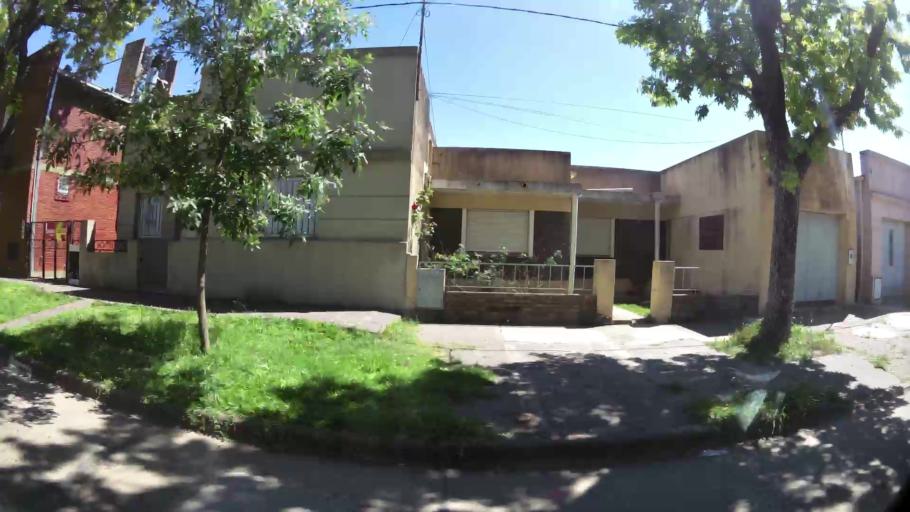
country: AR
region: Santa Fe
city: Esperanza
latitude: -31.4394
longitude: -60.9281
